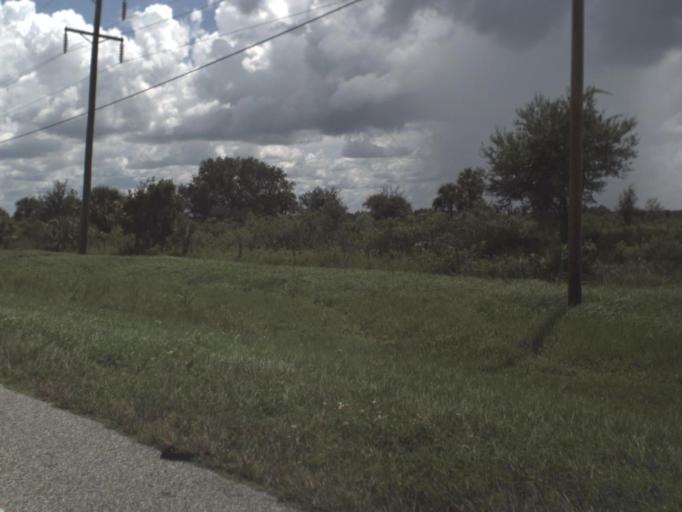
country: US
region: Florida
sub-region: Polk County
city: Babson Park
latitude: 27.8409
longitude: -81.3554
